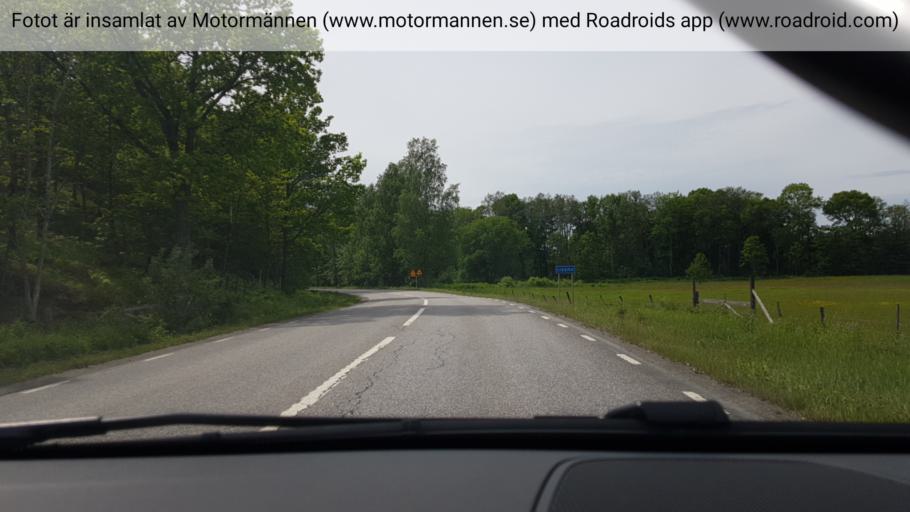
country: SE
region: Stockholm
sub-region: Haninge Kommun
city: Jordbro
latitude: 59.1771
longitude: 18.0785
